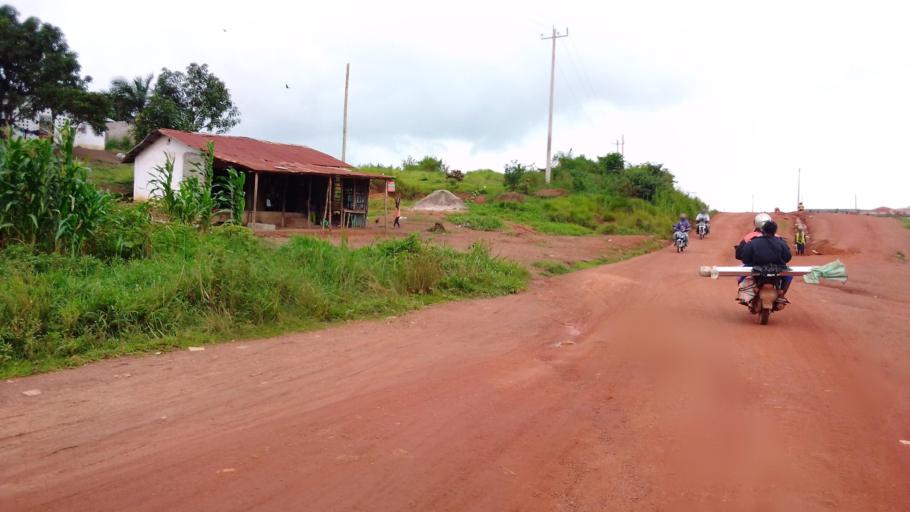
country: SL
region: Eastern Province
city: Kenema
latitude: 7.8392
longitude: -11.1825
